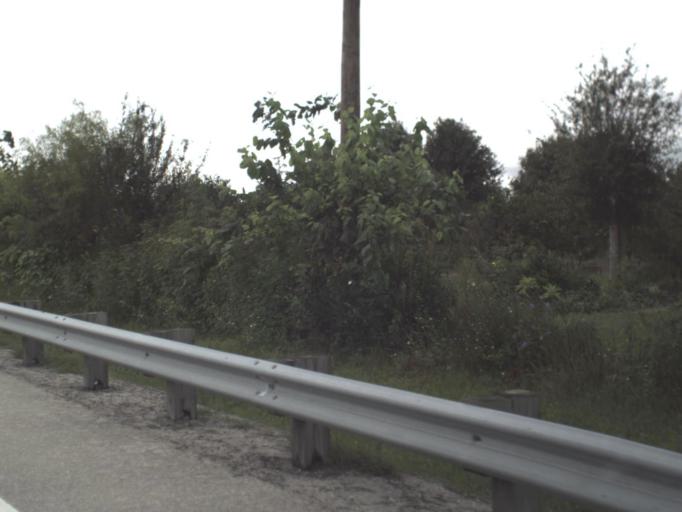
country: US
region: Florida
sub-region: Hardee County
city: Bowling Green
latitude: 27.5949
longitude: -81.8395
